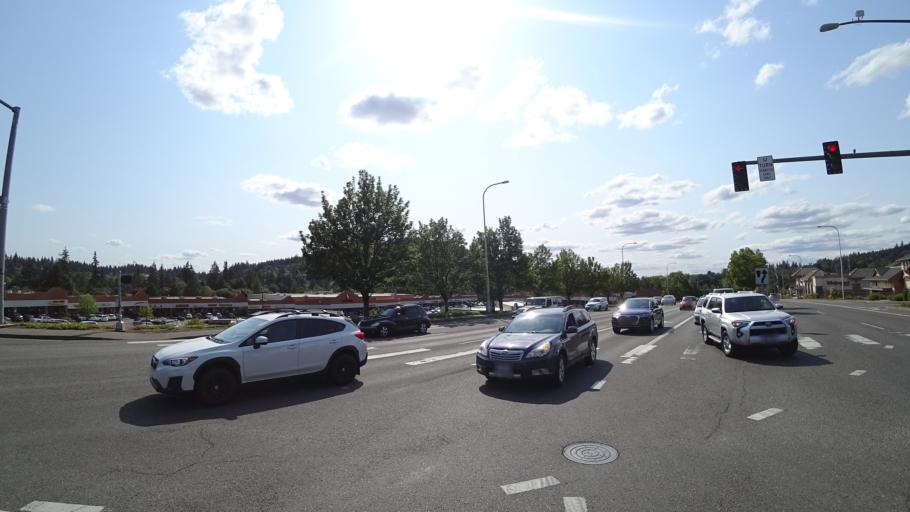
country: US
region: Oregon
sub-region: Clackamas County
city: Sunnyside
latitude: 45.4289
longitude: -122.5381
